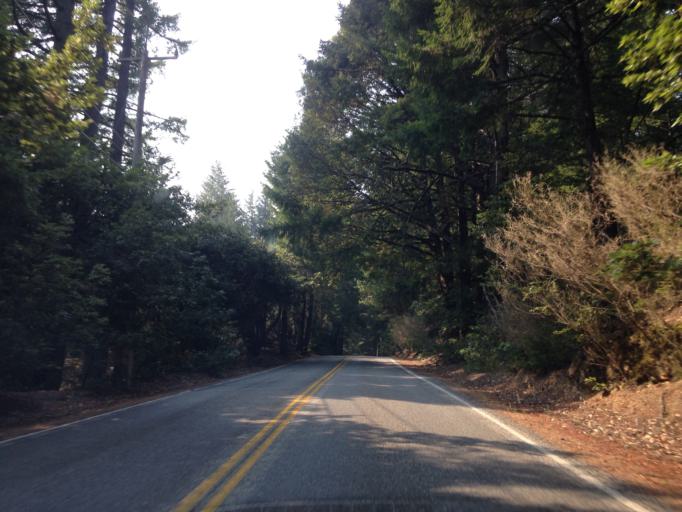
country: US
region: California
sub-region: San Mateo County
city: Woodside
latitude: 37.4141
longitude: -122.3115
